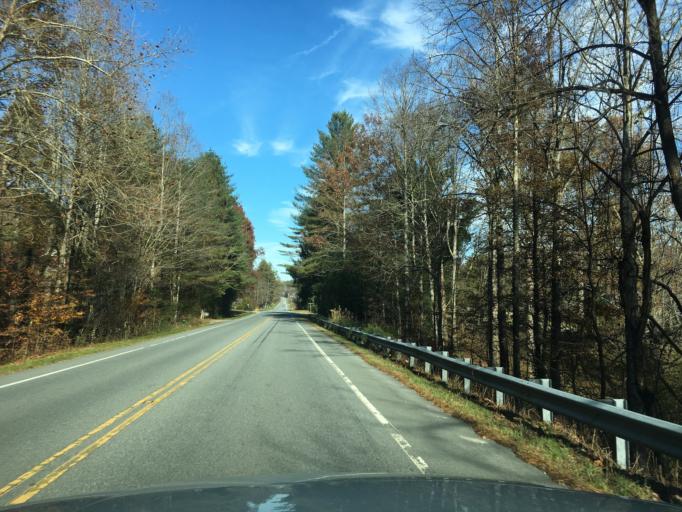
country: US
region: North Carolina
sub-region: Henderson County
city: Etowah
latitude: 35.2763
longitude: -82.6339
